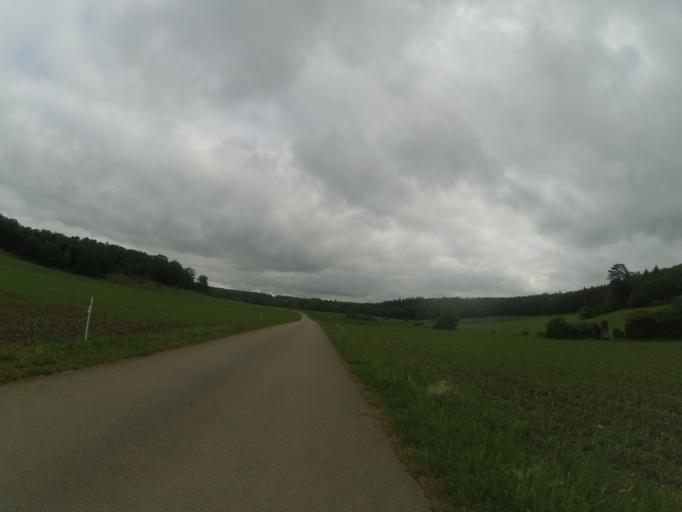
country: DE
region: Baden-Wuerttemberg
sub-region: Tuebingen Region
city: Bernstadt
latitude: 48.5113
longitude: 10.0315
